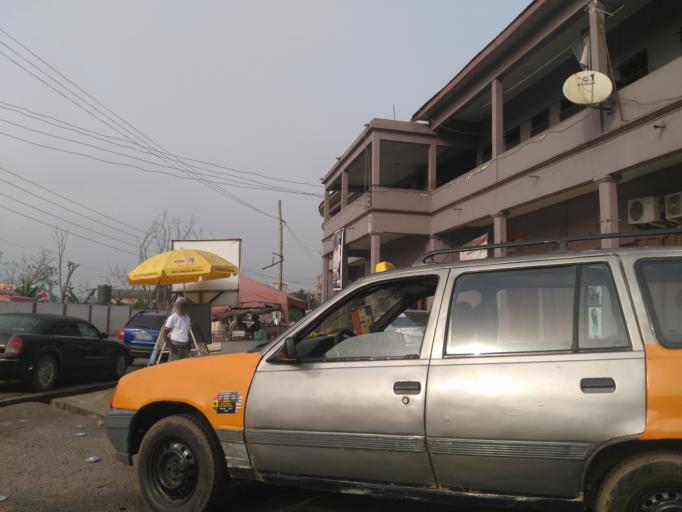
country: GH
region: Ashanti
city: Kumasi
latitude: 6.6905
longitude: -1.6122
